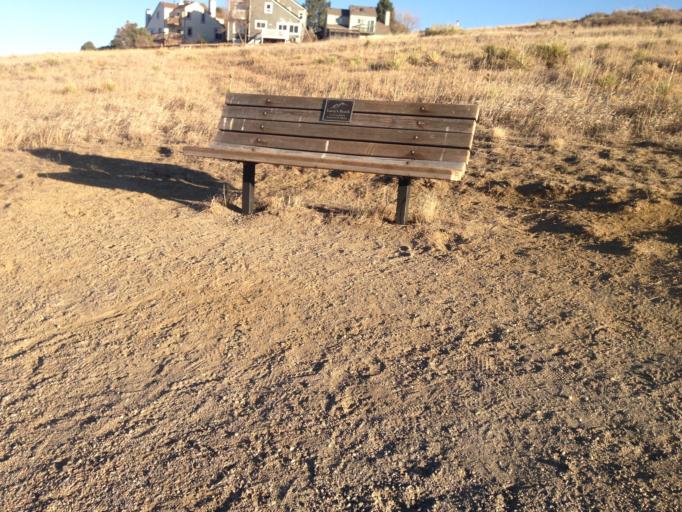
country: US
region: Colorado
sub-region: Broomfield County
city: Broomfield
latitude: 39.9354
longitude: -105.0986
